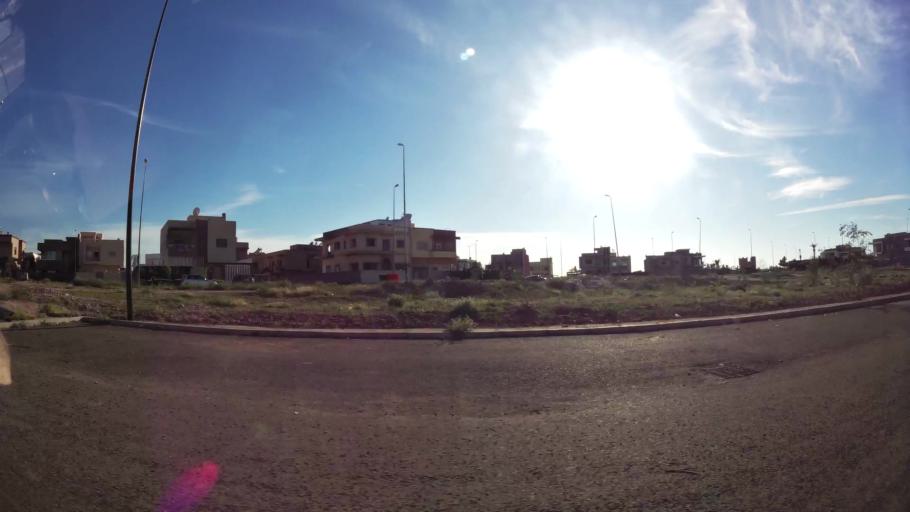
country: MA
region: Marrakech-Tensift-Al Haouz
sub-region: Marrakech
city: Marrakesh
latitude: 31.6728
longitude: -8.0718
